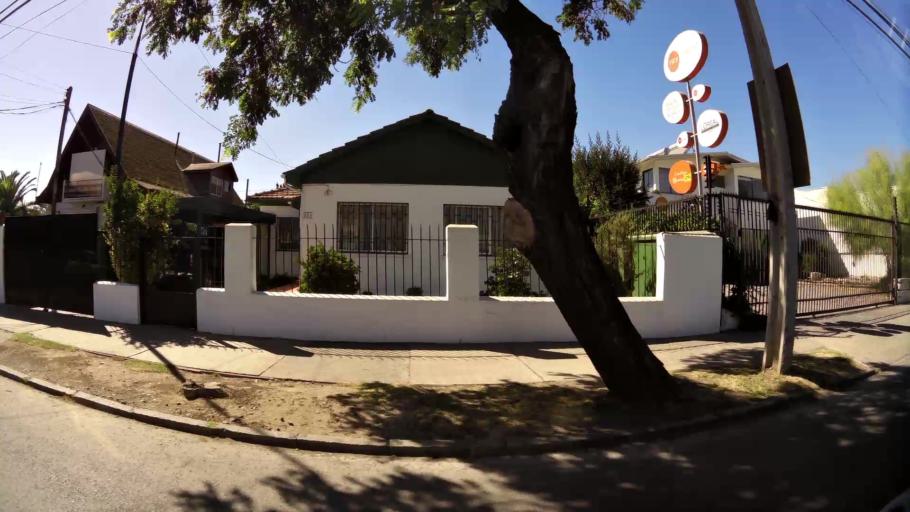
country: CL
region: O'Higgins
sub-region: Provincia de Cachapoal
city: Rancagua
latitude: -34.1782
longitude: -70.7440
